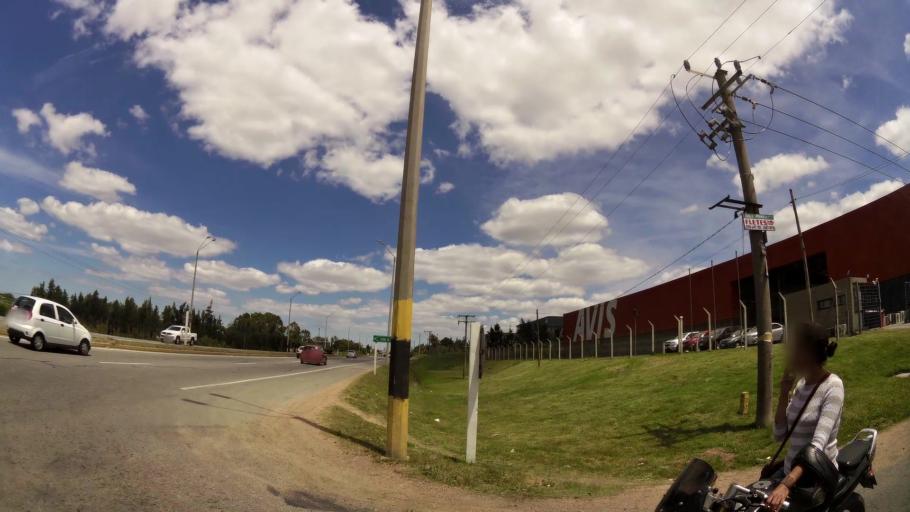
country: UY
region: Canelones
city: Colonia Nicolich
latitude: -34.8266
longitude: -56.0010
